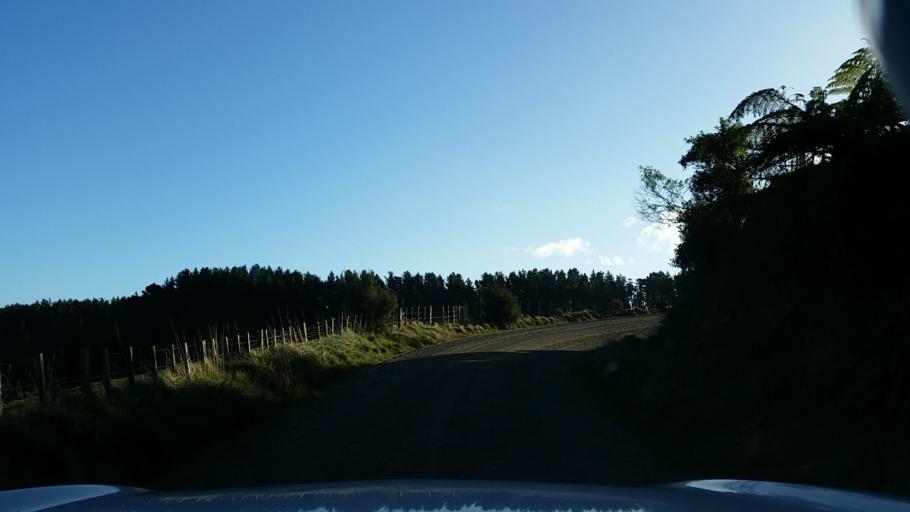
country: NZ
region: Taranaki
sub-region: South Taranaki District
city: Patea
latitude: -39.6666
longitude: 174.5248
